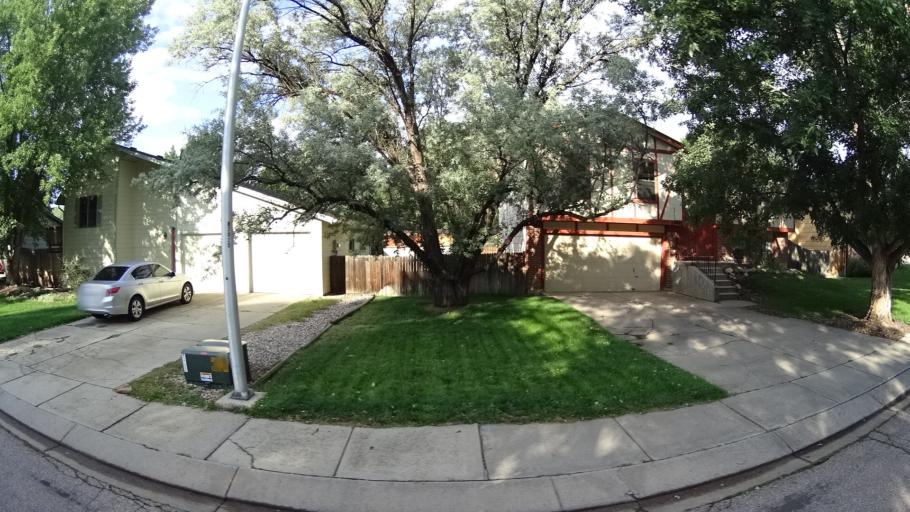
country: US
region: Colorado
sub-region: El Paso County
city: Manitou Springs
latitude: 38.9094
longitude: -104.8583
